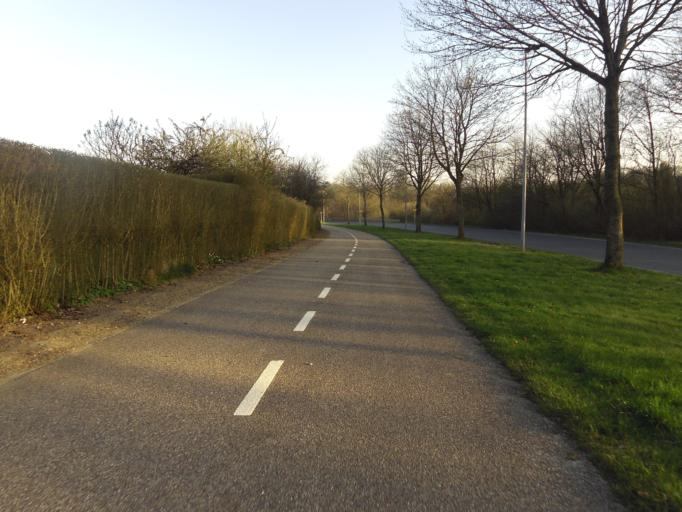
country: DK
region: South Denmark
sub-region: Vejen Kommune
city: Vejen
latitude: 55.4810
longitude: 9.1254
